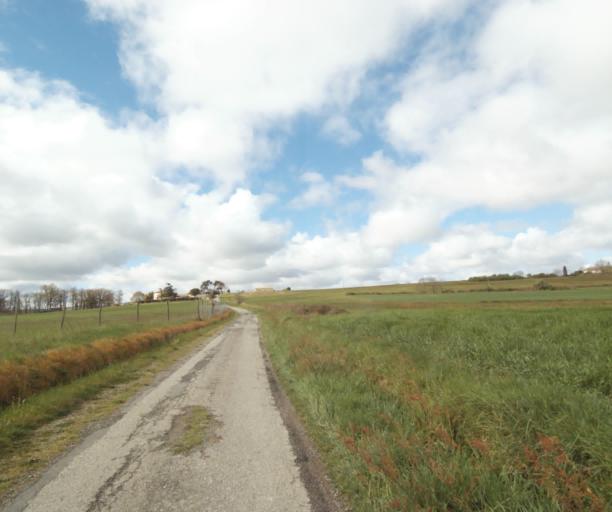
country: FR
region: Midi-Pyrenees
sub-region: Departement de l'Ariege
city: Saverdun
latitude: 43.2166
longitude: 1.5678
